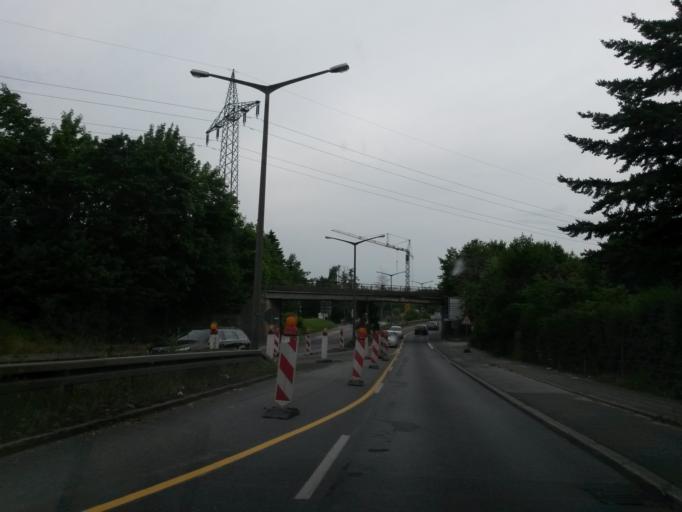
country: DE
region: Bavaria
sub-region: Regierungsbezirk Mittelfranken
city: Grossreuth bei Schweinau
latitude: 49.4368
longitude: 10.9929
